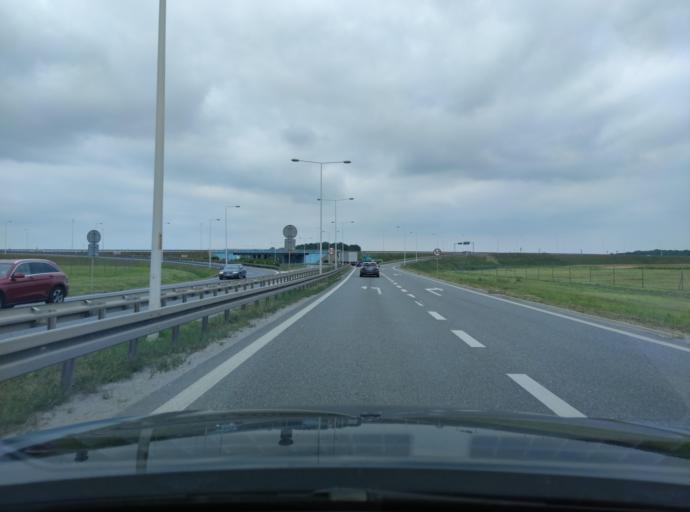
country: PL
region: Lower Silesian Voivodeship
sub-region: Powiat wroclawski
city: Tyniec Maly
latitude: 51.0305
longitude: 16.9360
